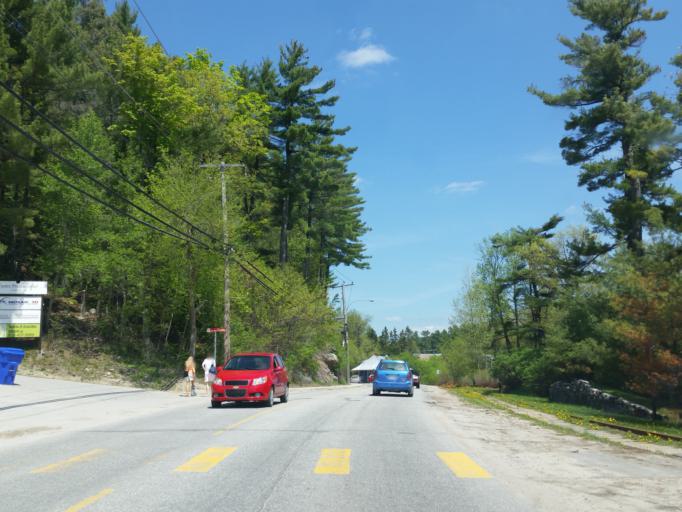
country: CA
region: Quebec
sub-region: Outaouais
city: Wakefield
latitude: 45.6377
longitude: -75.9299
